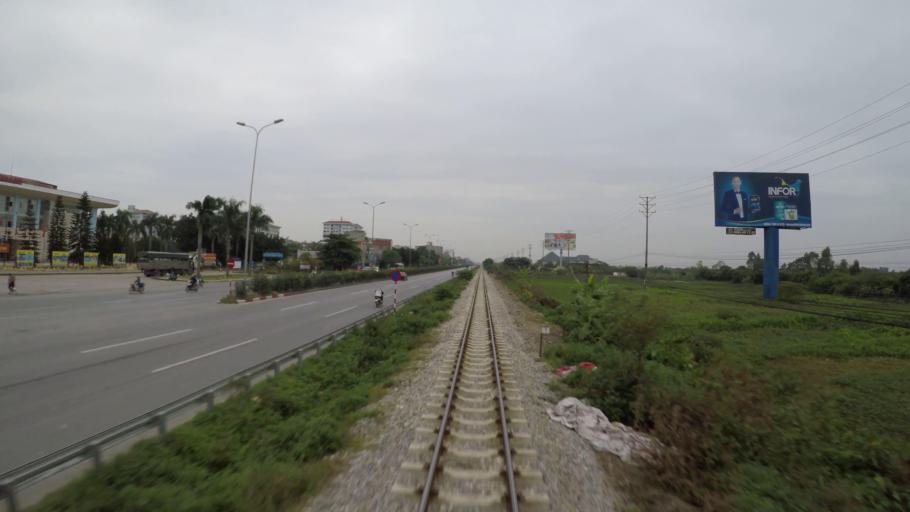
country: VN
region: Hung Yen
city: Nhu Quynh
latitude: 20.9852
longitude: 105.9780
